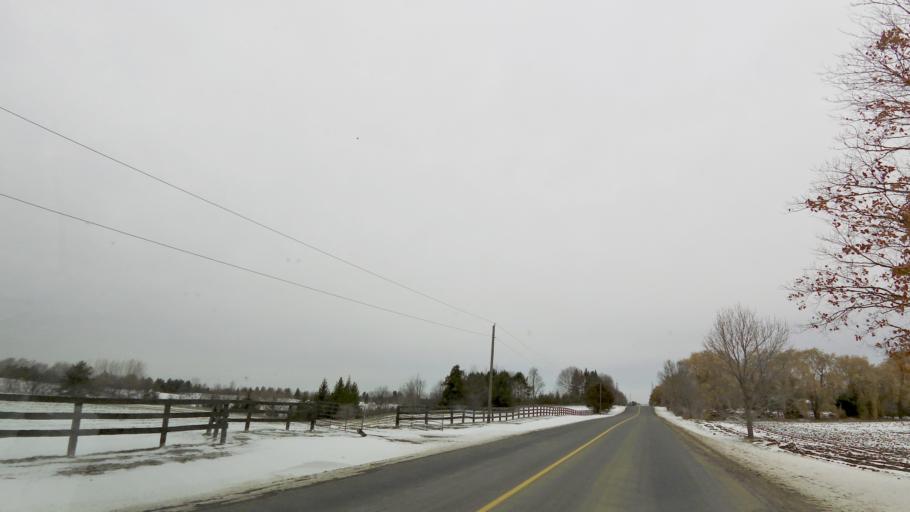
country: CA
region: Ontario
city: Bradford West Gwillimbury
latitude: 43.9712
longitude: -79.6435
